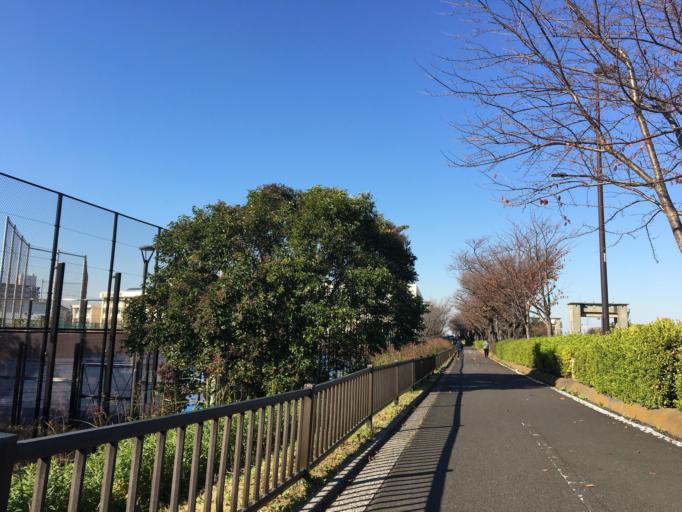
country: JP
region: Tokyo
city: Urayasu
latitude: 35.6992
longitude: 139.9176
